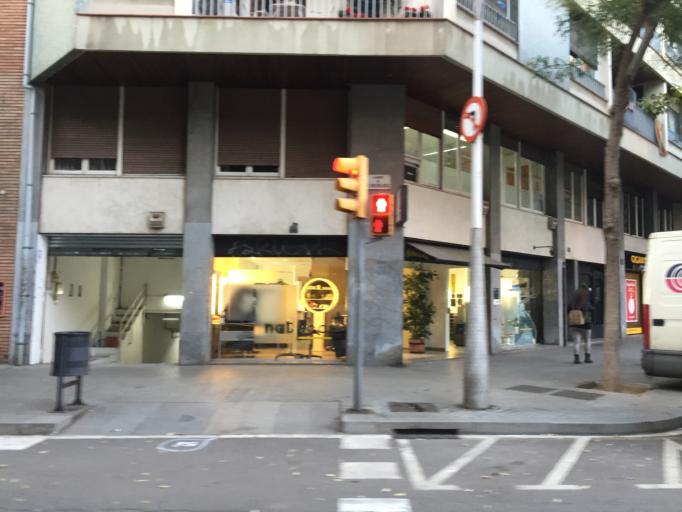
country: ES
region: Catalonia
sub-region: Provincia de Barcelona
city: Sants-Montjuic
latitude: 41.3785
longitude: 2.1583
